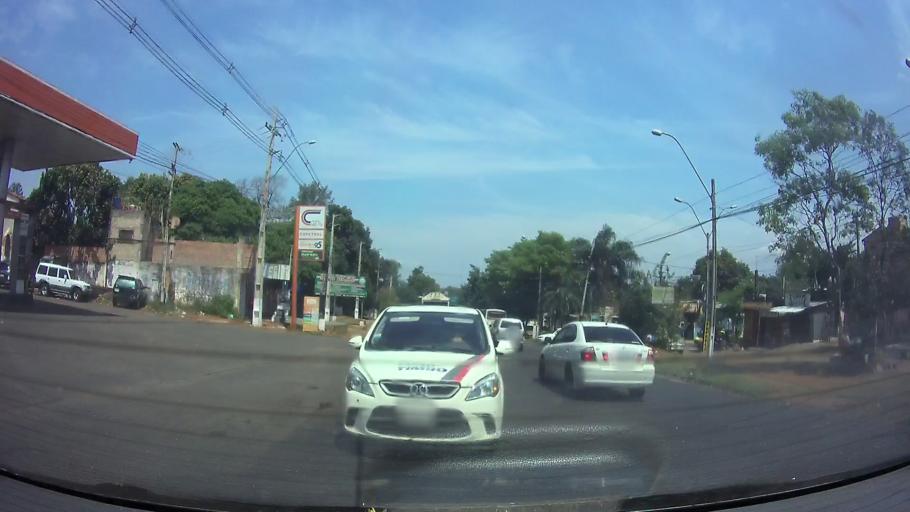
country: PY
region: Central
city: Capiata
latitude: -25.3901
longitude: -57.4698
